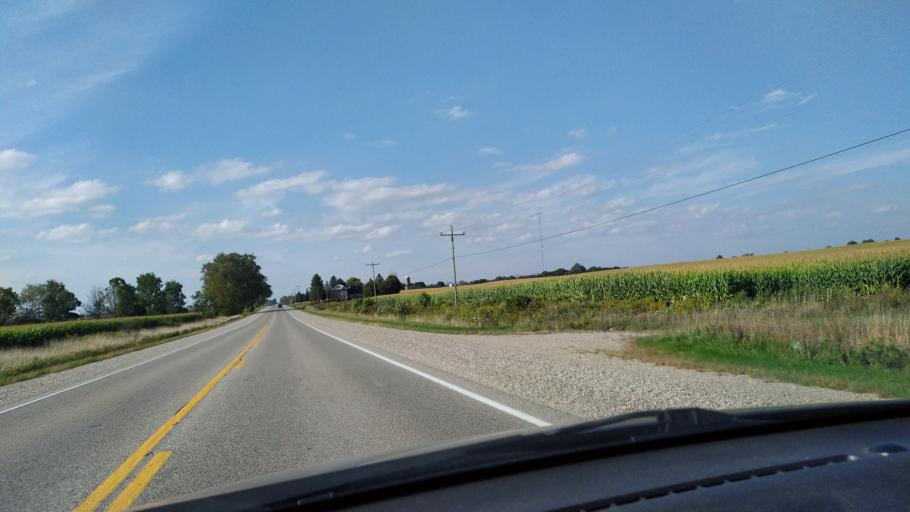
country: CA
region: Ontario
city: Ingersoll
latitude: 43.1295
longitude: -80.8880
